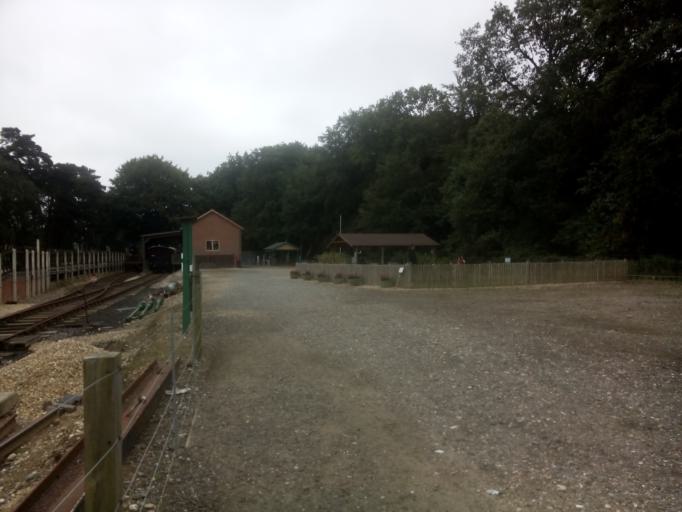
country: GB
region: England
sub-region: Norfolk
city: Briston
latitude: 52.9156
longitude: 1.1134
